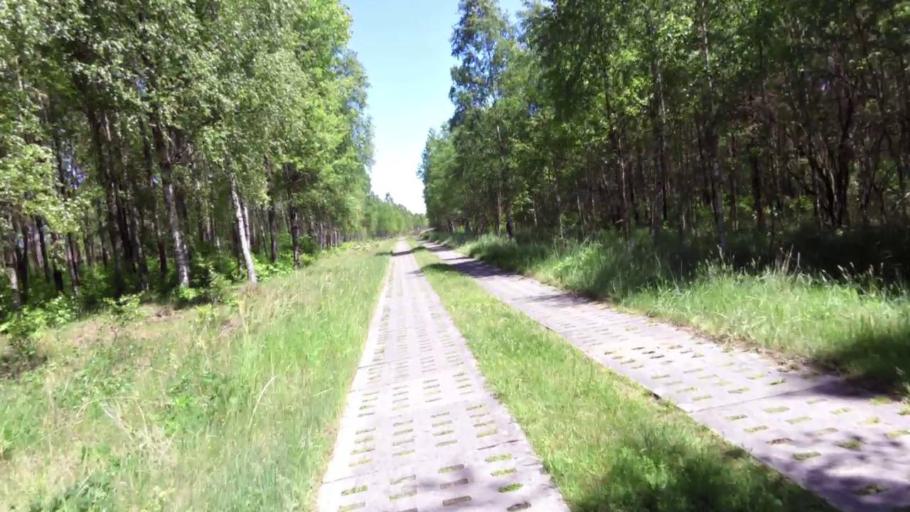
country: PL
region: West Pomeranian Voivodeship
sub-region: Powiat szczecinecki
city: Borne Sulinowo
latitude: 53.5679
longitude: 16.6265
